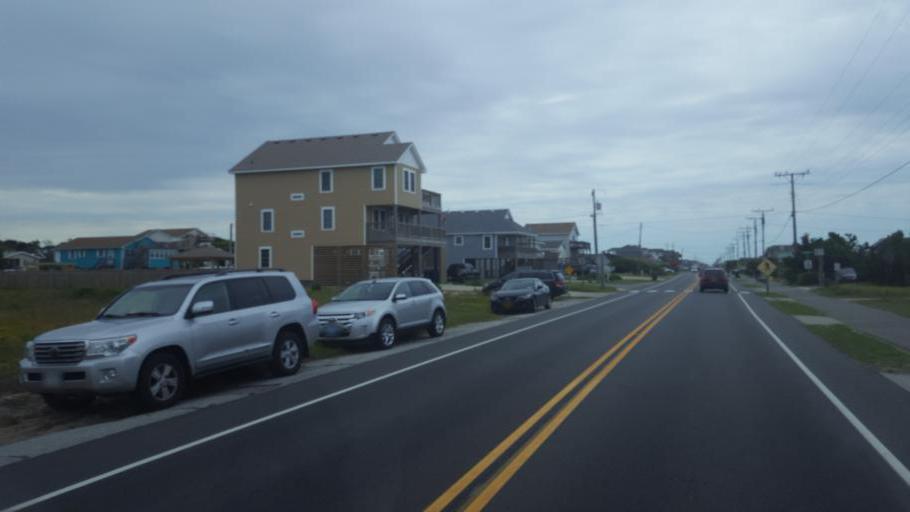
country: US
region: North Carolina
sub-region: Dare County
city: Nags Head
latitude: 35.9803
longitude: -75.6371
